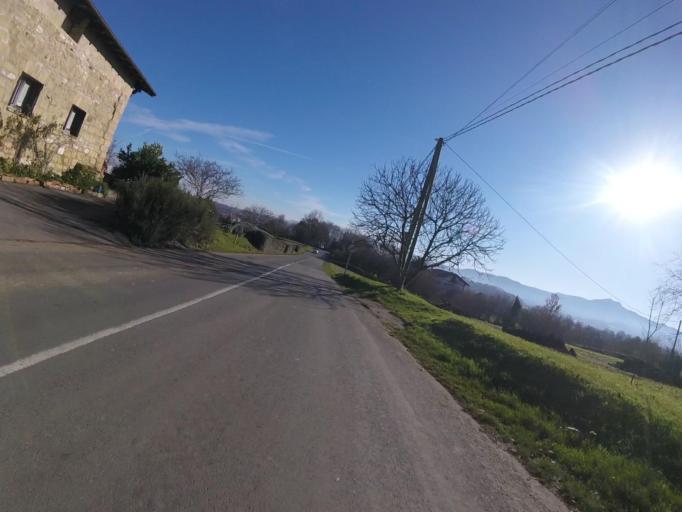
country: ES
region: Basque Country
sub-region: Provincia de Guipuzcoa
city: Fuenterrabia
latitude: 43.3649
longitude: -1.8088
